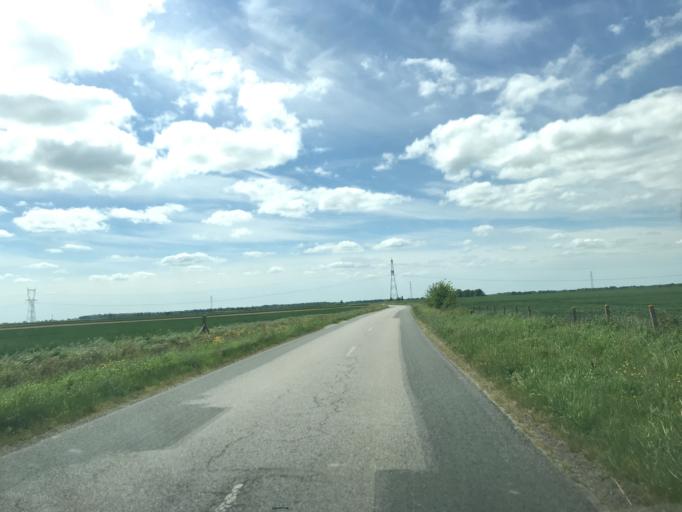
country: FR
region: Haute-Normandie
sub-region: Departement de l'Eure
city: Le Neubourg
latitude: 49.1480
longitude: 0.8602
